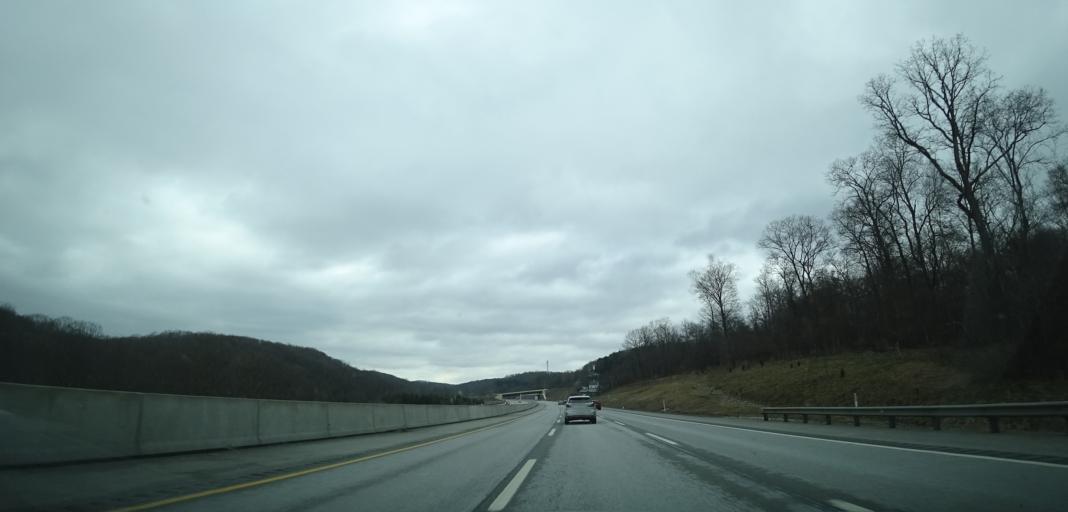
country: US
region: Pennsylvania
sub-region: Allegheny County
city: Gibsonia
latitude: 40.6258
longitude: -79.9830
